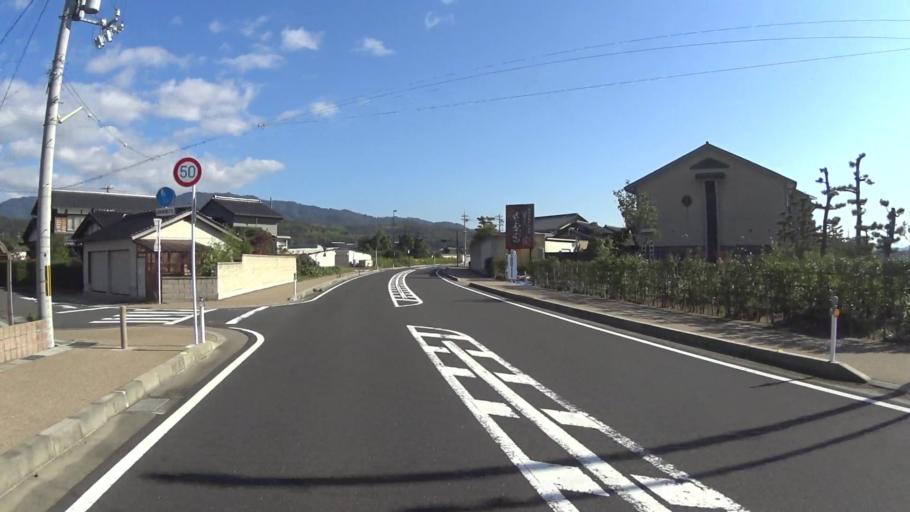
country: JP
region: Kyoto
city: Miyazu
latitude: 35.5688
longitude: 135.1577
